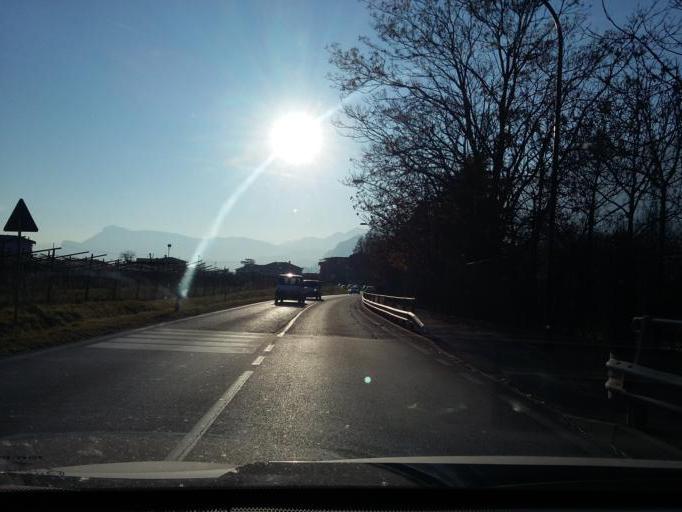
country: IT
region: Trentino-Alto Adige
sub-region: Provincia di Trento
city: Villa Lagarina
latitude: 45.9126
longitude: 11.0439
